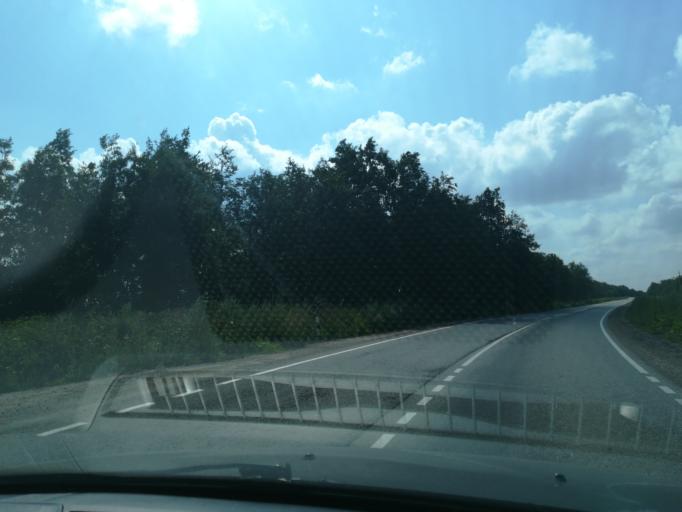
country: RU
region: Leningrad
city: Kopor'ye
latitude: 59.6965
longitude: 29.0568
